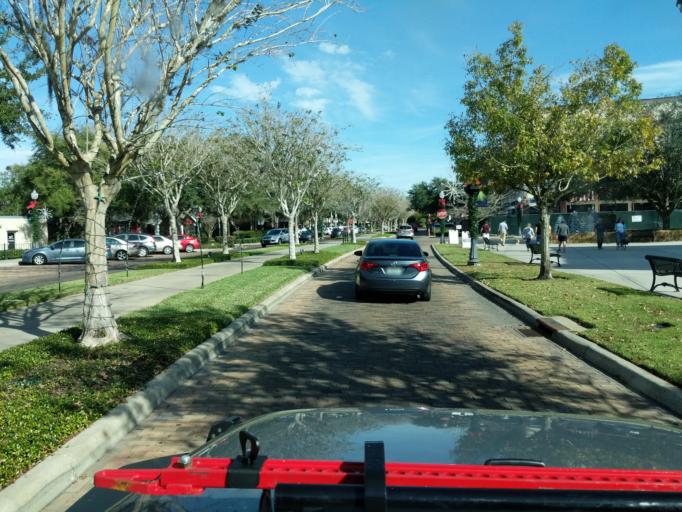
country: US
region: Florida
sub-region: Orange County
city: Winter Garden
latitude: 28.5650
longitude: -81.5897
